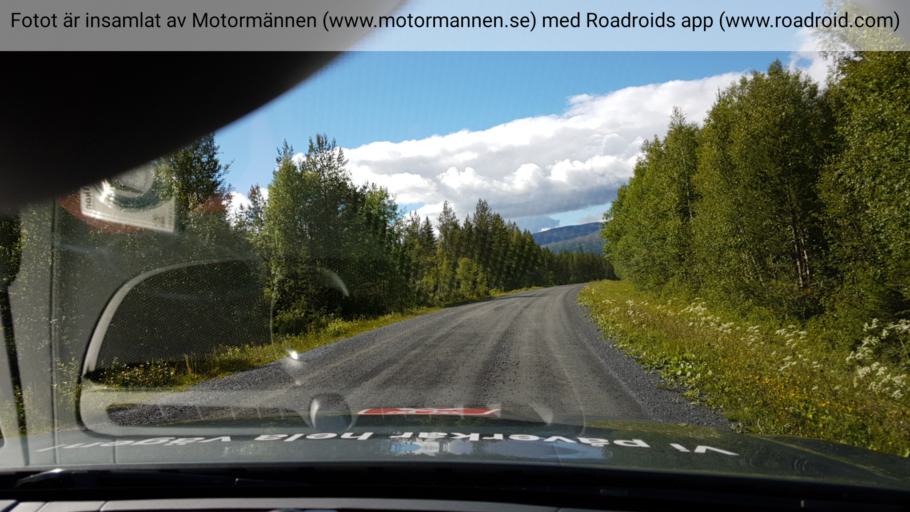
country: SE
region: Jaemtland
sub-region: Krokoms Kommun
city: Valla
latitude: 63.0847
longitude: 13.9188
